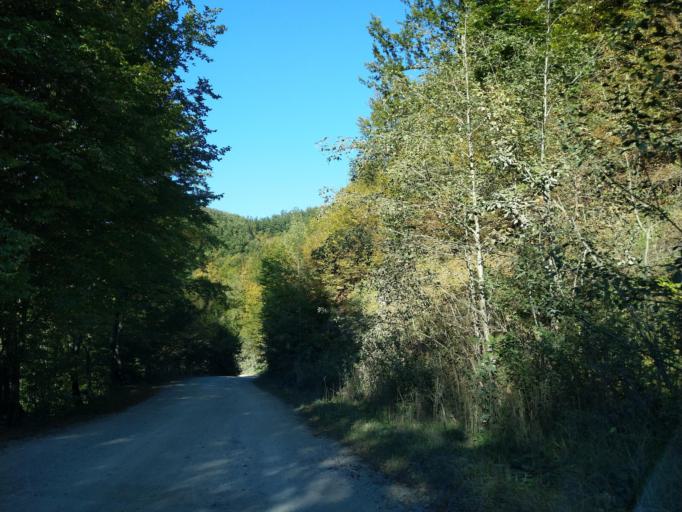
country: RS
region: Central Serbia
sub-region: Moravicki Okrug
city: Ivanjica
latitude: 43.4776
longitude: 20.2382
